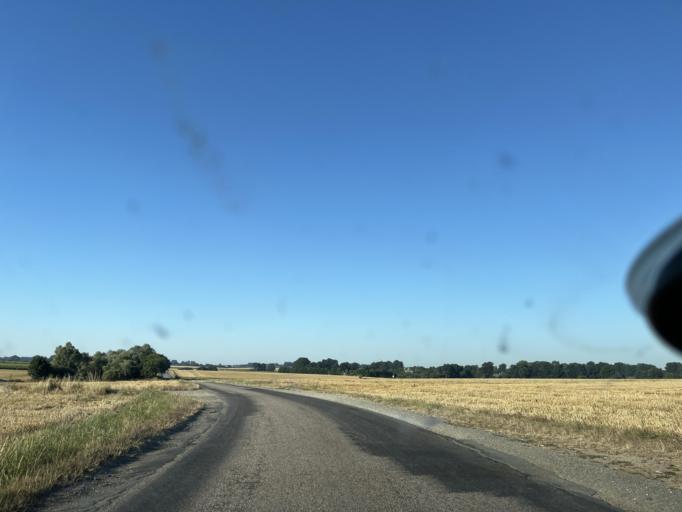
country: FR
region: Haute-Normandie
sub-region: Departement de la Seine-Maritime
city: Fauville-en-Caux
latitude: 49.6281
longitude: 0.6251
